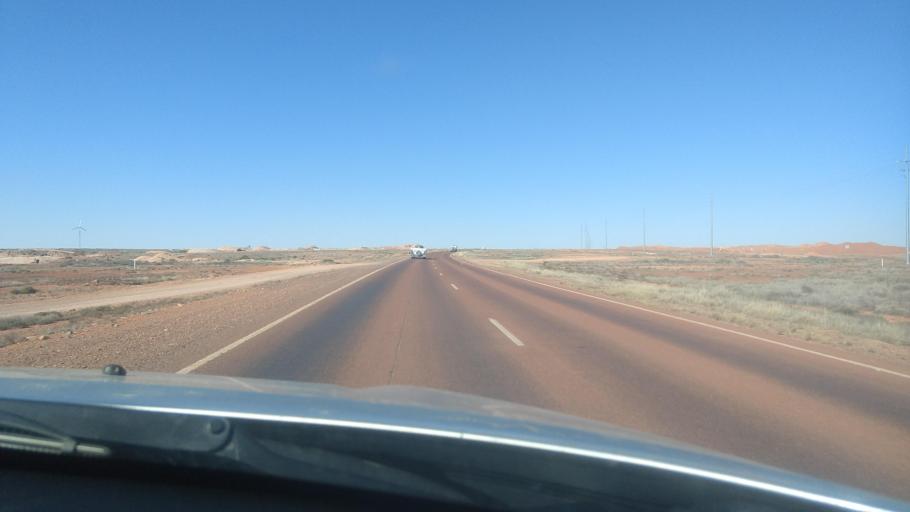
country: AU
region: South Australia
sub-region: Coober Pedy
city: Coober Pedy
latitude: -29.0258
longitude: 134.7744
